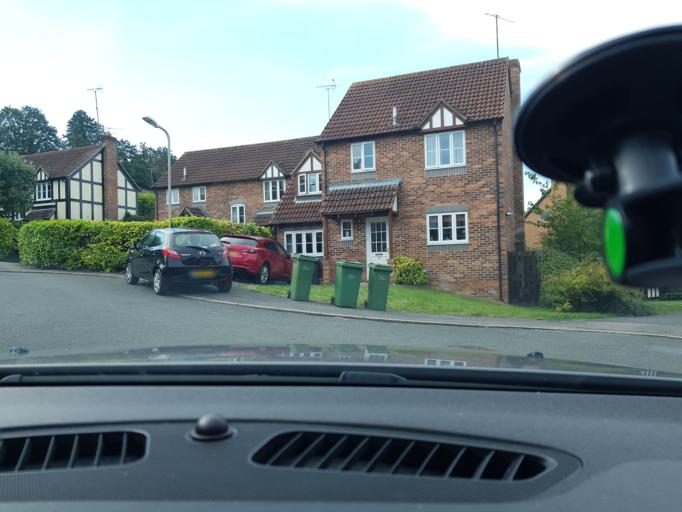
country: GB
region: England
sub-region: West Berkshire
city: Hungerford
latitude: 51.4137
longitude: -1.5224
